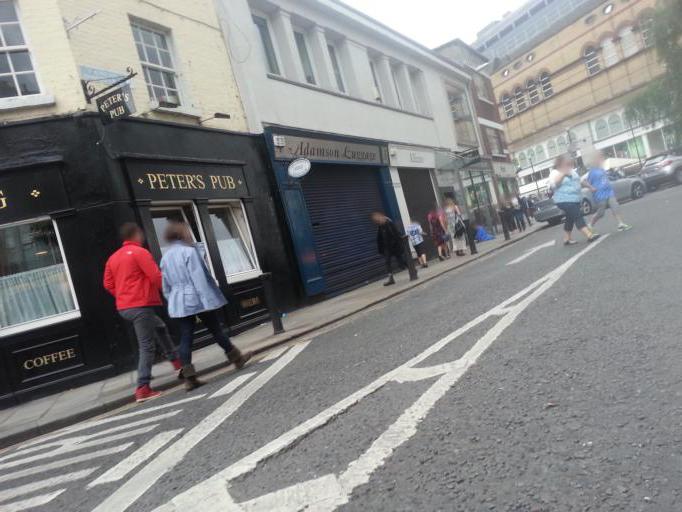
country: IE
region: Leinster
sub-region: Dublin City
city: Dublin
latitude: 53.3409
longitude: -6.2635
